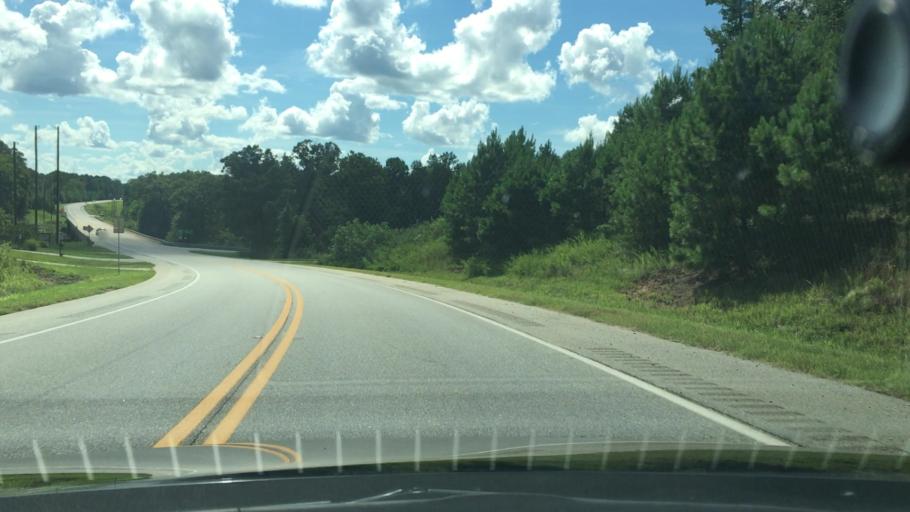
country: US
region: Georgia
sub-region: Butts County
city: Indian Springs
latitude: 33.3071
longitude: -83.8334
